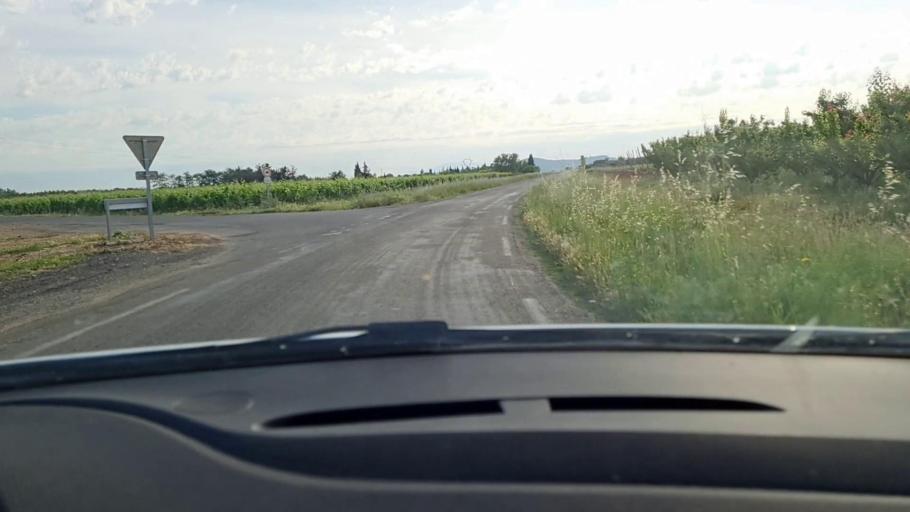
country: FR
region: Languedoc-Roussillon
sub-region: Departement du Gard
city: Jonquieres-Saint-Vincent
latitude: 43.8148
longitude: 4.5498
